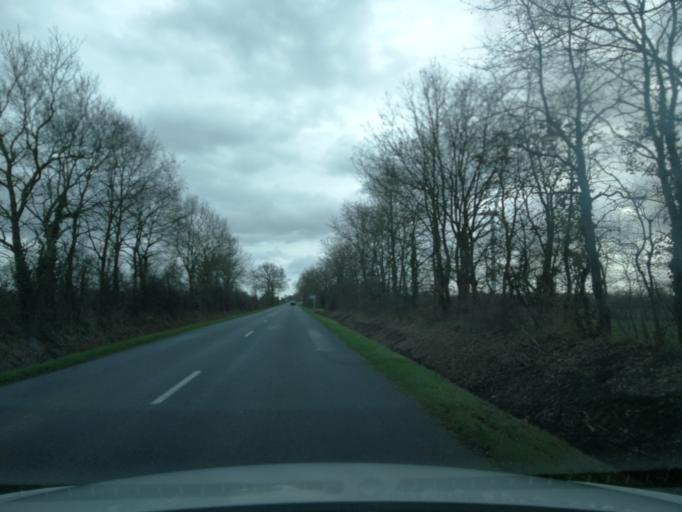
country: FR
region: Pays de la Loire
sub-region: Departement de la Loire-Atlantique
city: La Planche
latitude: 47.0056
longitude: -1.4728
